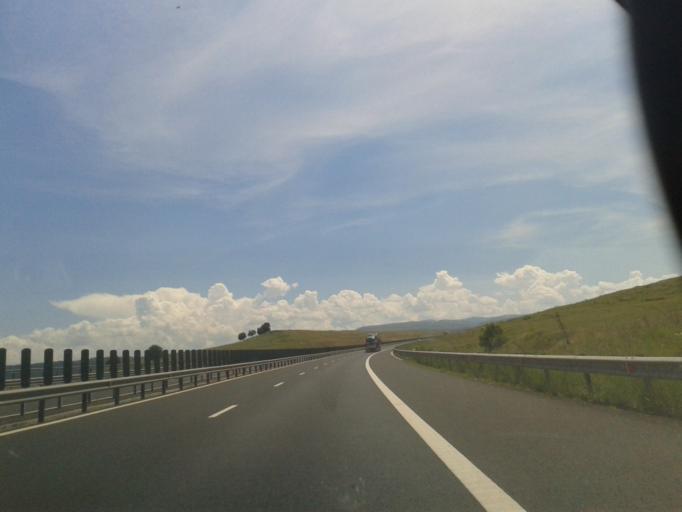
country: RO
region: Sibiu
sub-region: Comuna Apoldu de Jos
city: Apoldu de Jos
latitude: 45.8625
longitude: 23.8798
